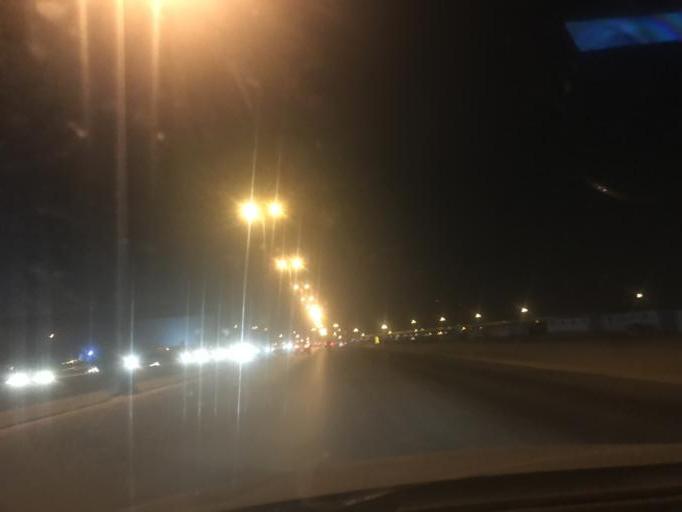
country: SA
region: Ar Riyad
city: Riyadh
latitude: 24.8312
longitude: 46.7295
